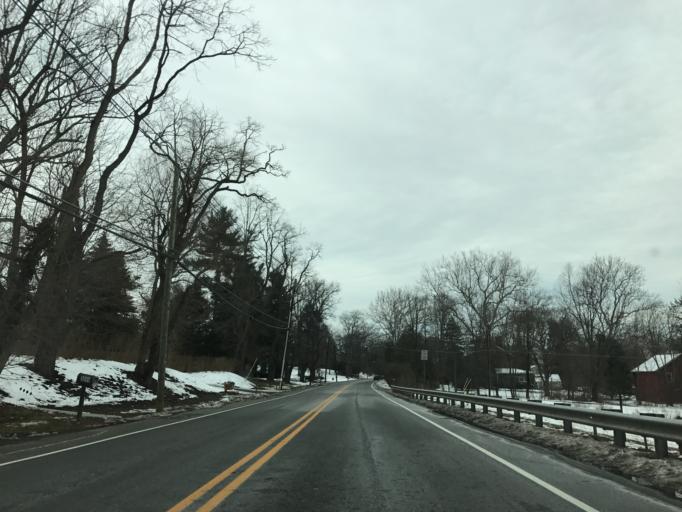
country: US
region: New Jersey
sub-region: Mercer County
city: Lawrenceville
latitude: 40.3069
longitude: -74.7202
